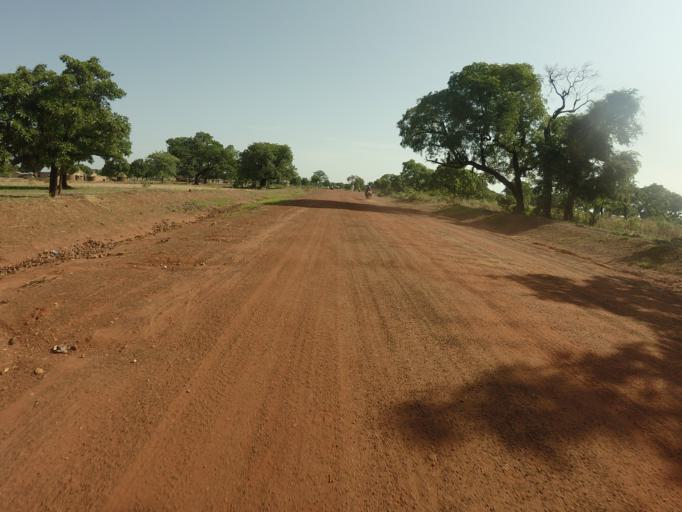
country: GH
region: Upper East
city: Bawku
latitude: 10.7824
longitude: -0.1887
